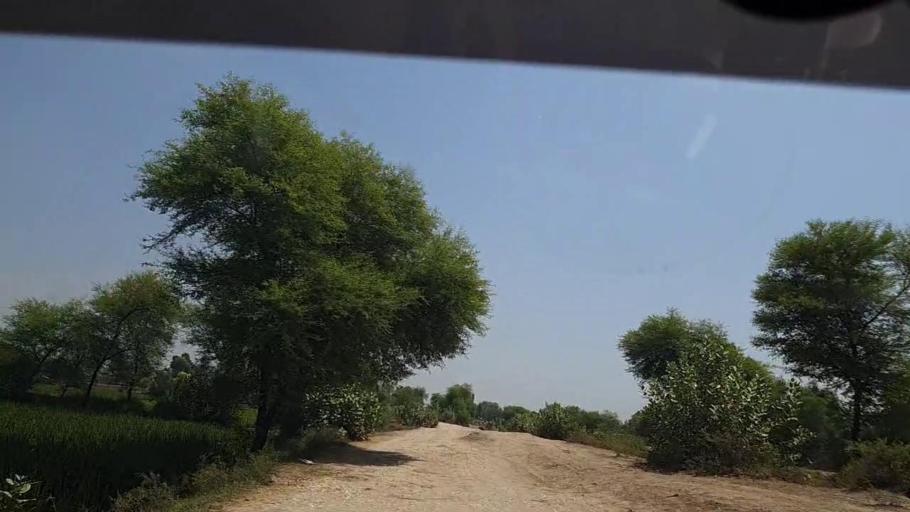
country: PK
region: Sindh
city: Ghauspur
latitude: 28.1686
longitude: 69.1225
